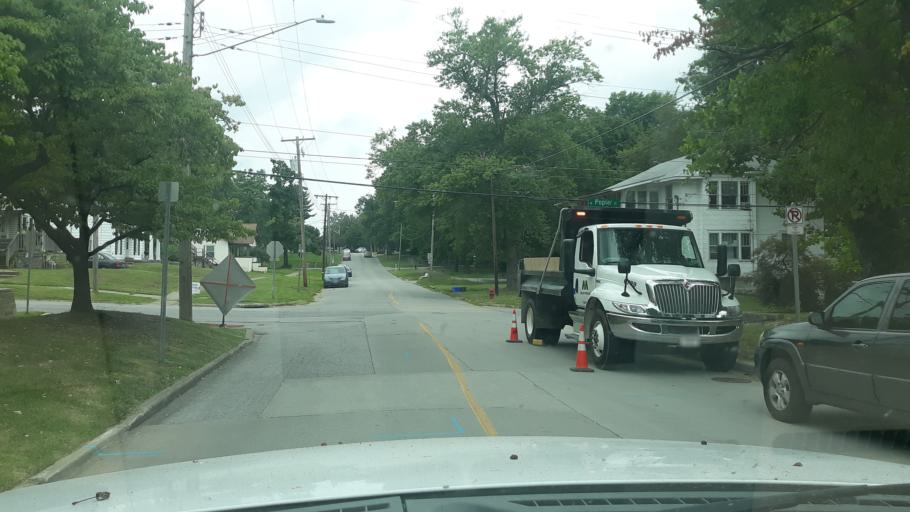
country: US
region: Illinois
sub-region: Jackson County
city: Carbondale
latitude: 37.7288
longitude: -89.2220
